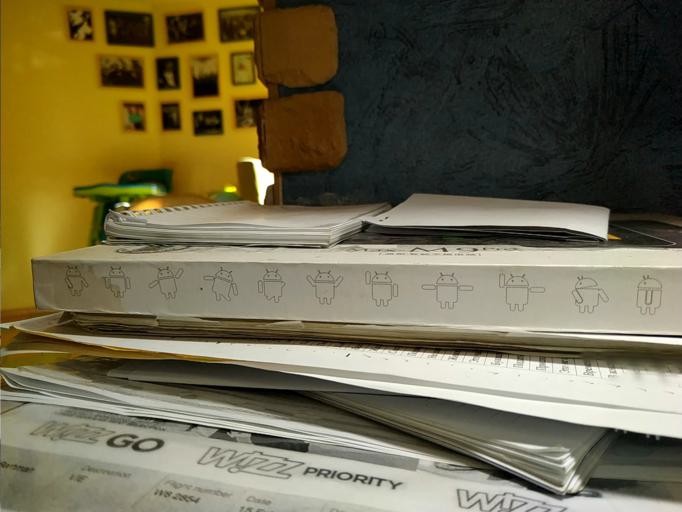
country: RU
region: Novgorod
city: Poddor'ye
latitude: 57.4970
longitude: 30.9502
